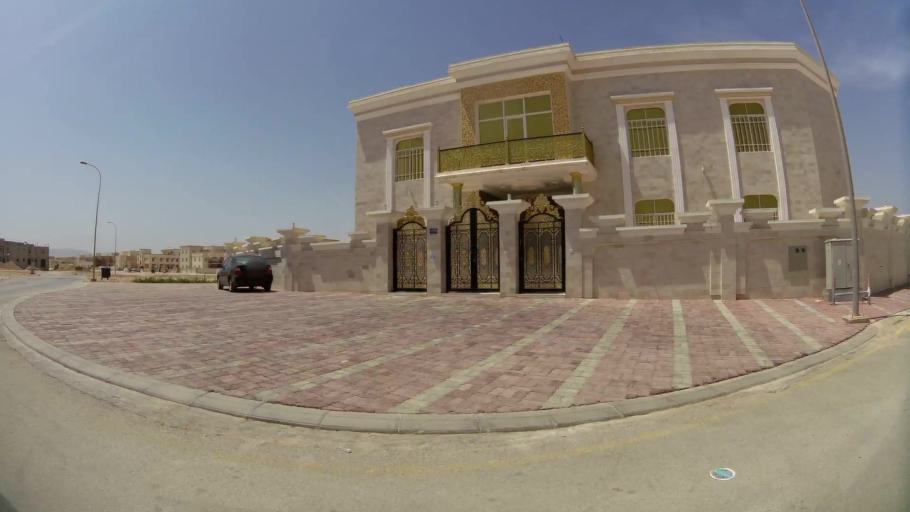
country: OM
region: Zufar
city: Salalah
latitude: 17.0589
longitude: 54.1620
